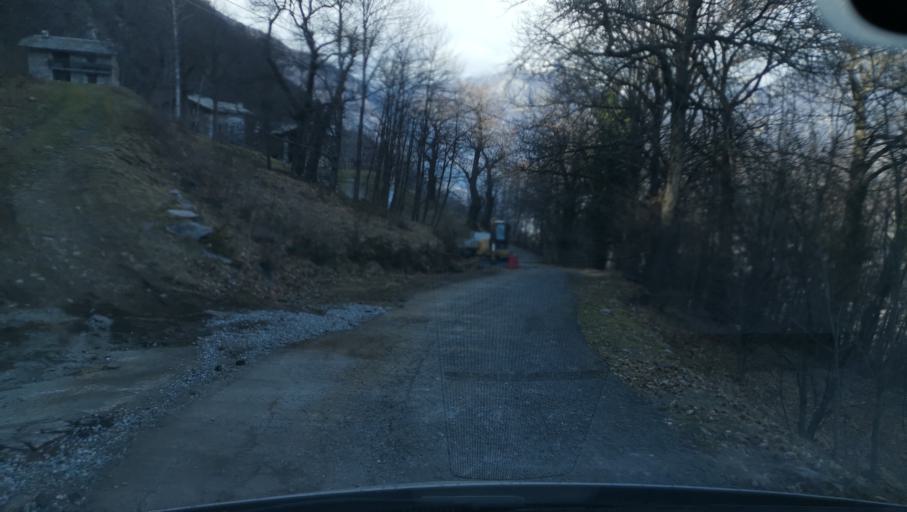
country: IT
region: Piedmont
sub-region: Provincia di Torino
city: Tavagnasco
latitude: 45.5358
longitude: 7.8177
